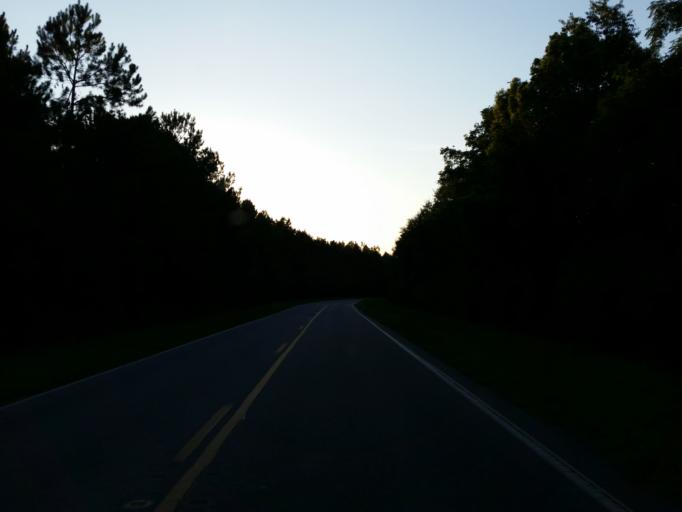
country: US
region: Georgia
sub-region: Berrien County
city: Nashville
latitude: 31.1991
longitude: -83.2260
